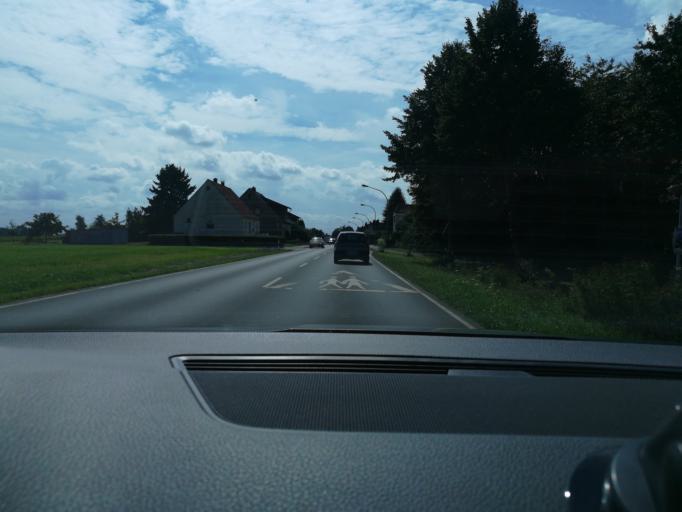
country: DE
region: North Rhine-Westphalia
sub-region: Regierungsbezirk Detmold
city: Huellhorst
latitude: 52.2853
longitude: 8.6661
